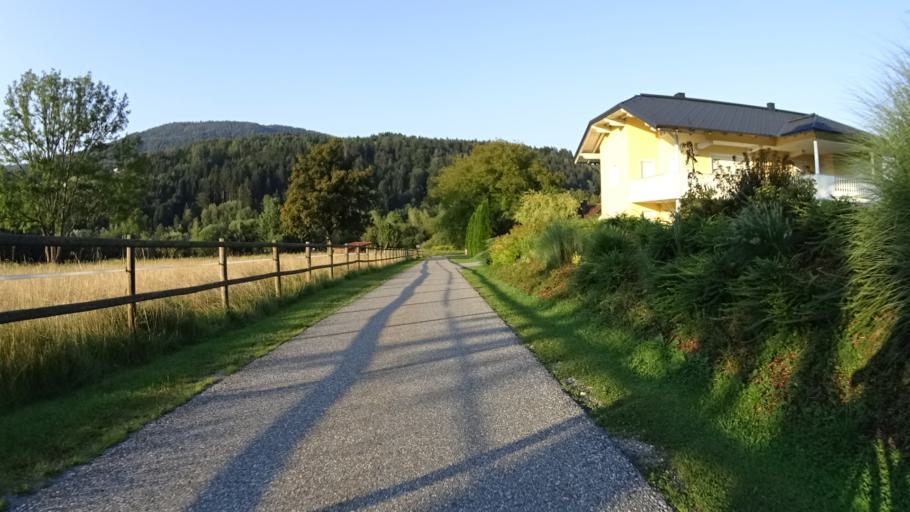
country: AT
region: Carinthia
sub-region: Politischer Bezirk Klagenfurt Land
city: Ludmannsdorf
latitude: 46.5359
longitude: 14.1091
